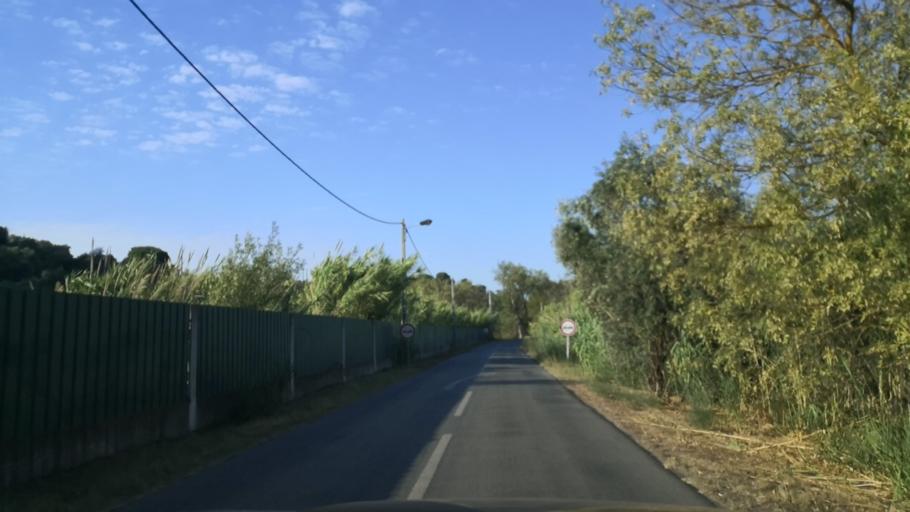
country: PT
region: Santarem
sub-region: Santarem
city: Santarem
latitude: 39.2580
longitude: -8.6694
